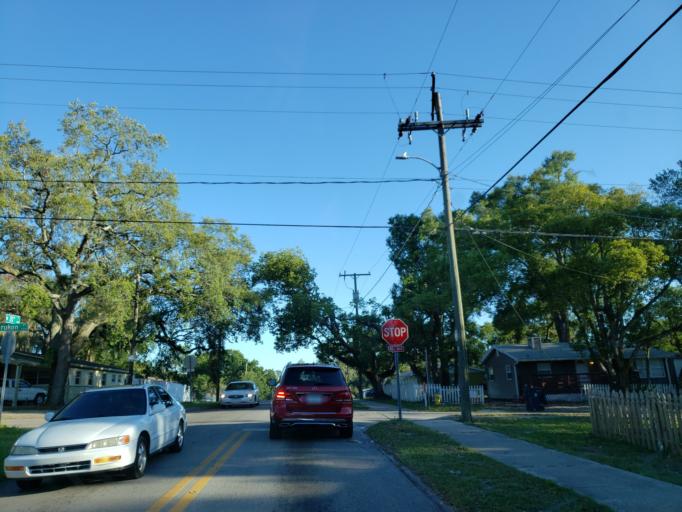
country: US
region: Florida
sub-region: Hillsborough County
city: University
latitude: 28.0292
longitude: -82.4368
